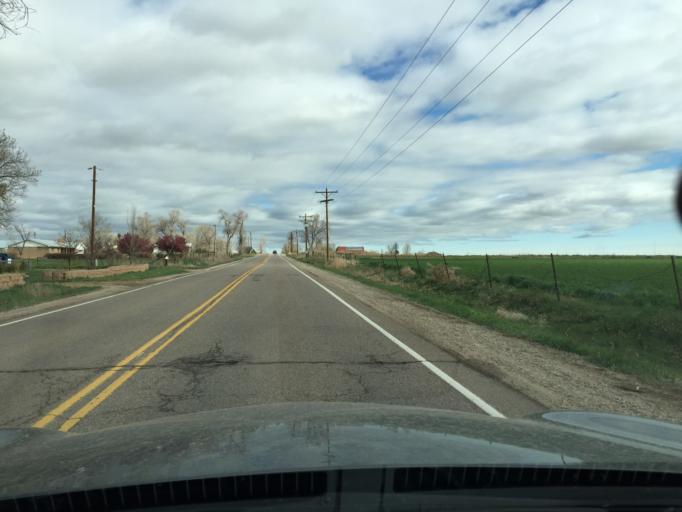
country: US
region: Colorado
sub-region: Adams County
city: Northglenn
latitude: 39.9696
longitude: -104.9971
